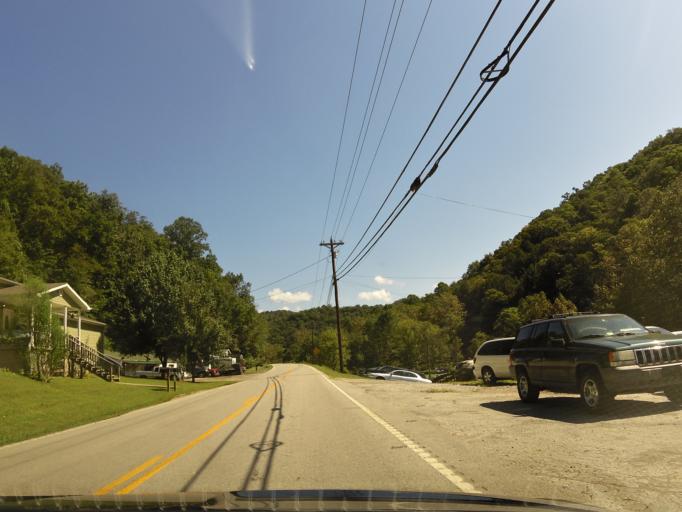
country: US
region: Kentucky
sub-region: Clay County
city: Manchester
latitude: 37.1519
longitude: -83.5965
